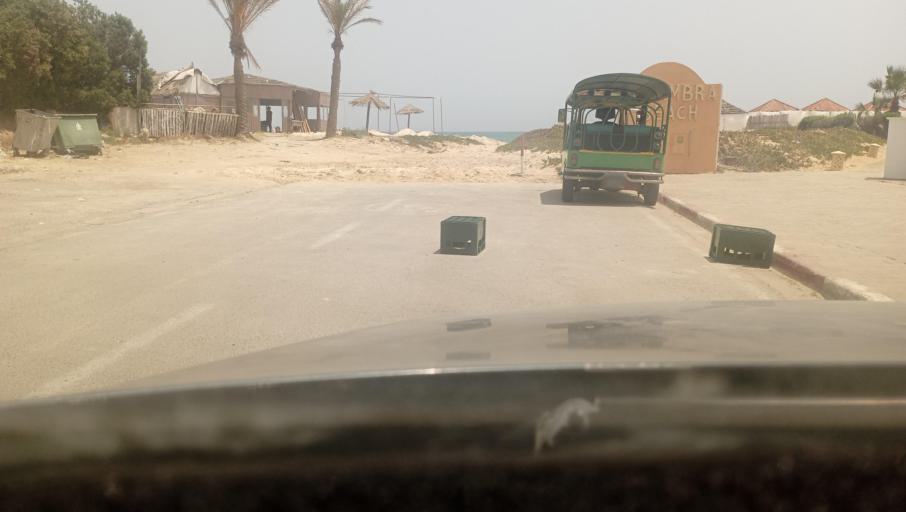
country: TN
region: Nabul
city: Al Hammamat
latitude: 36.3538
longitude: 10.5292
